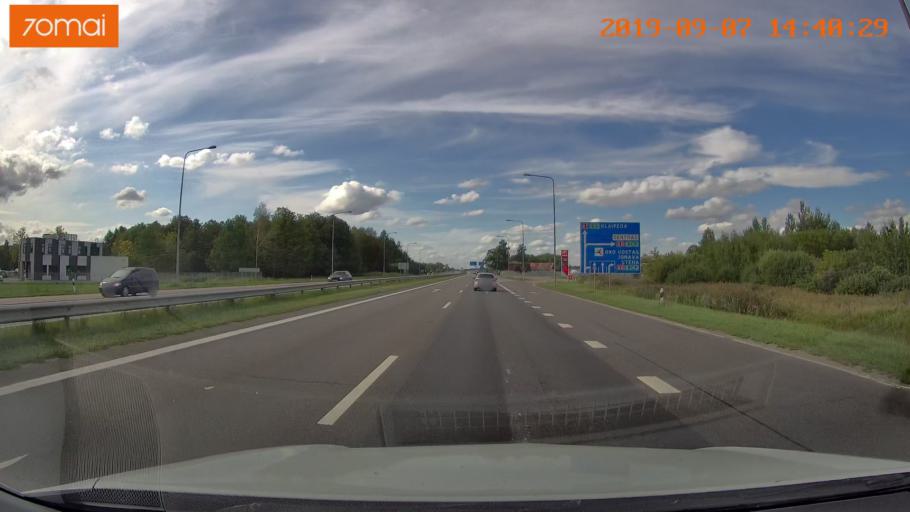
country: LT
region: Kauno apskritis
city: Dainava (Kaunas)
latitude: 54.9315
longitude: 23.9983
